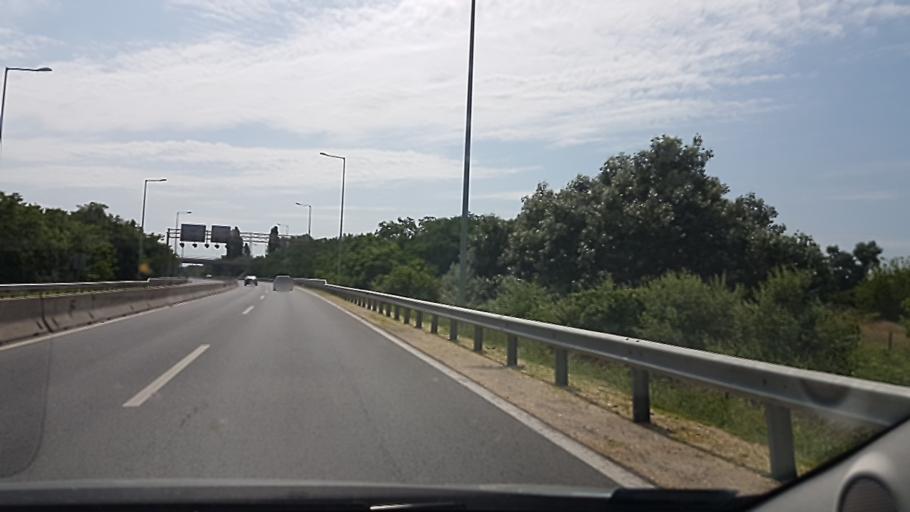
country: HU
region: Budapest
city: Budapest XXIII. keruelet
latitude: 47.3948
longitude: 19.1589
